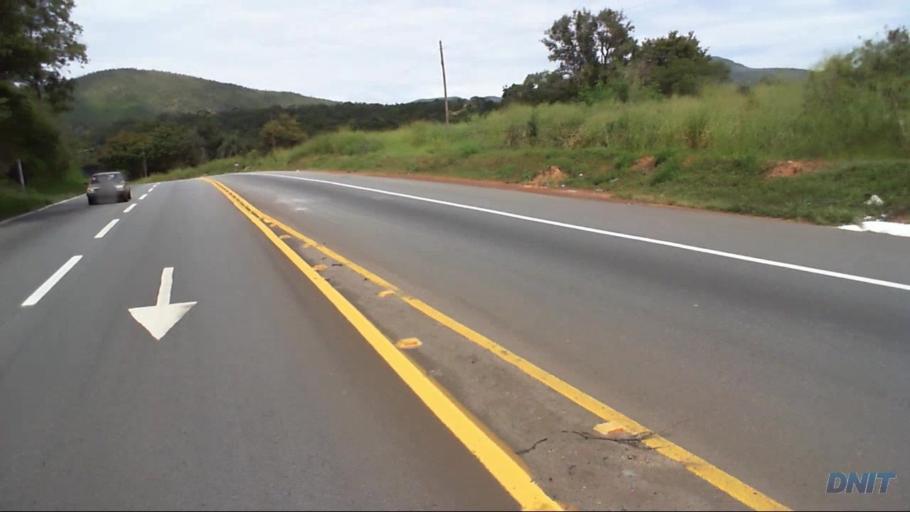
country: BR
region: Minas Gerais
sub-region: Santa Luzia
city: Santa Luzia
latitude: -19.7994
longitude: -43.7531
